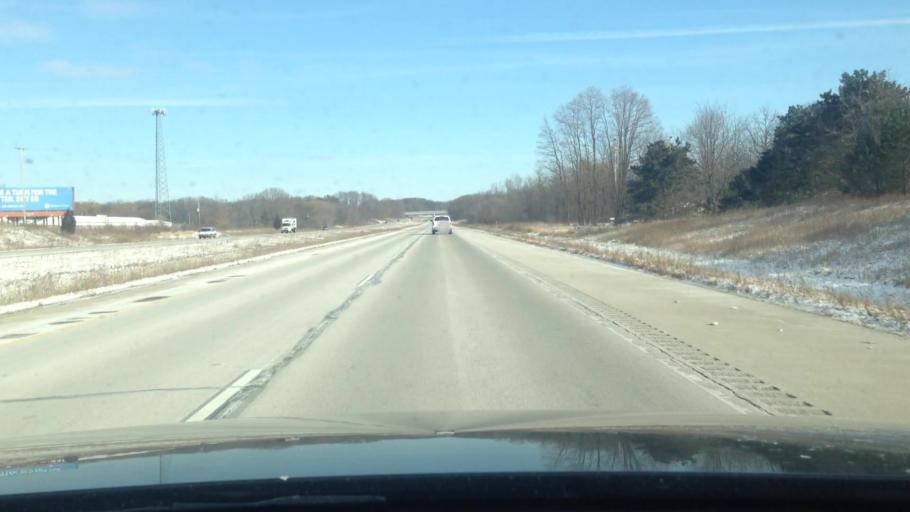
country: US
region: Wisconsin
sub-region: Walworth County
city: Potter Lake
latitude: 42.8166
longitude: -88.3624
